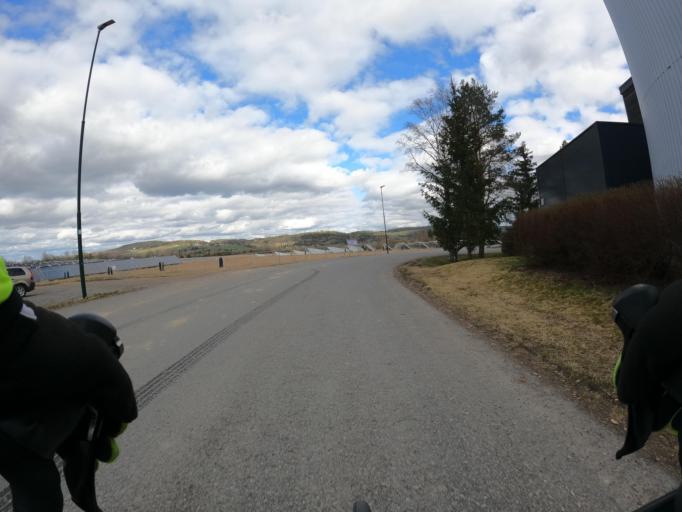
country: NO
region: Akershus
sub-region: Skedsmo
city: Leirsund
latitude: 59.9719
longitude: 11.0738
